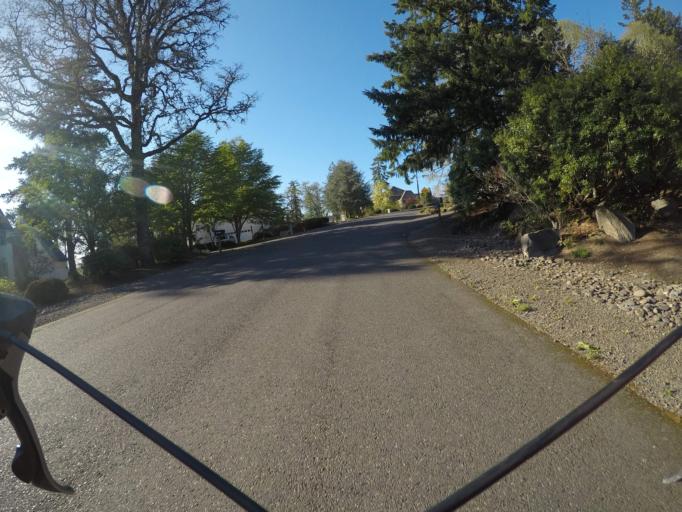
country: US
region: Oregon
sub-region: Washington County
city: Aloha
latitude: 45.4492
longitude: -122.8805
